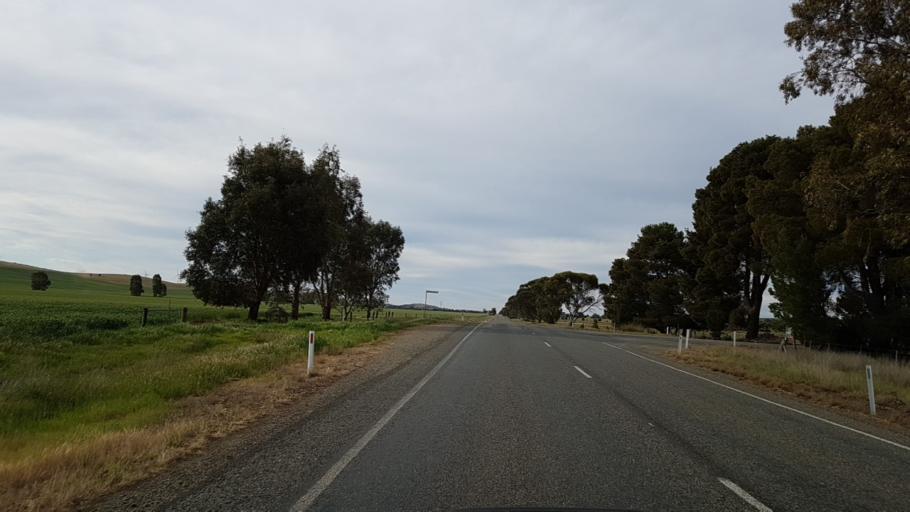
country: AU
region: South Australia
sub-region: Northern Areas
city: Jamestown
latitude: -33.1859
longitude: 138.6106
